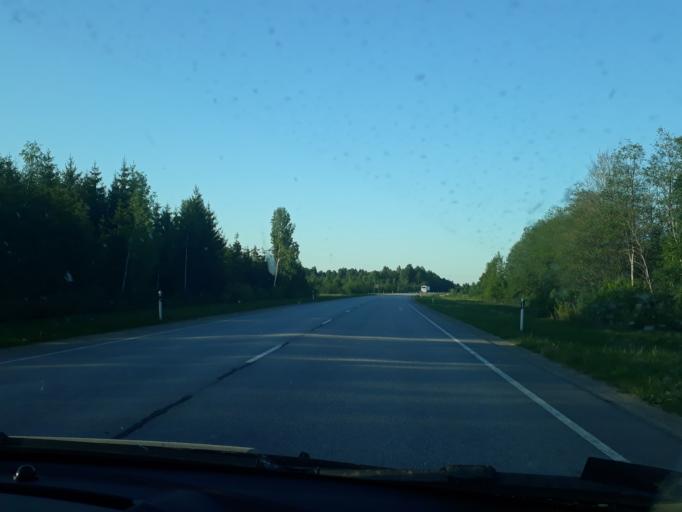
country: EE
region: Paernumaa
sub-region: Sindi linn
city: Sindi
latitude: 58.4657
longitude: 24.7053
